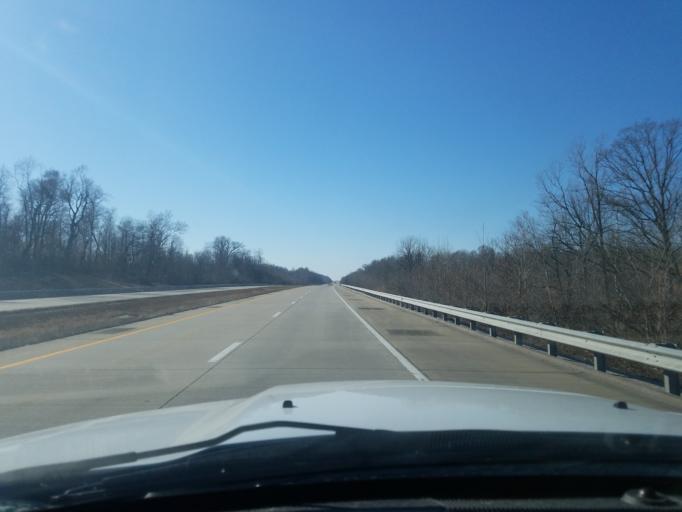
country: US
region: Indiana
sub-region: Warrick County
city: Newburgh
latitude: 37.7585
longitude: -87.3357
